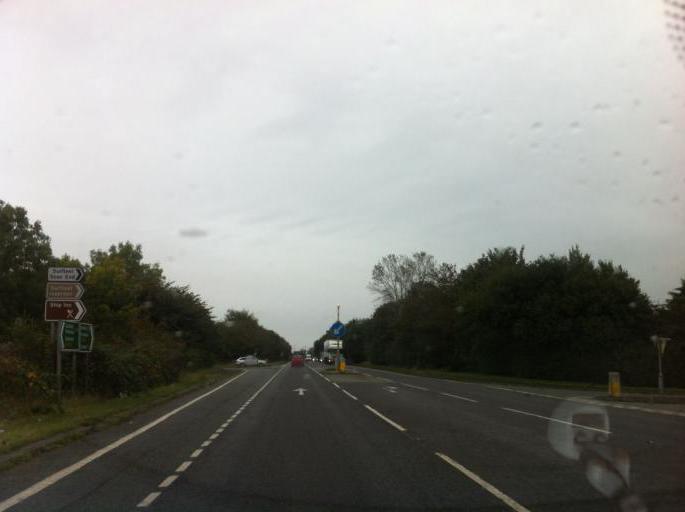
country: GB
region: England
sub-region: Lincolnshire
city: Gosberton
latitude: 52.8408
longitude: -0.1226
